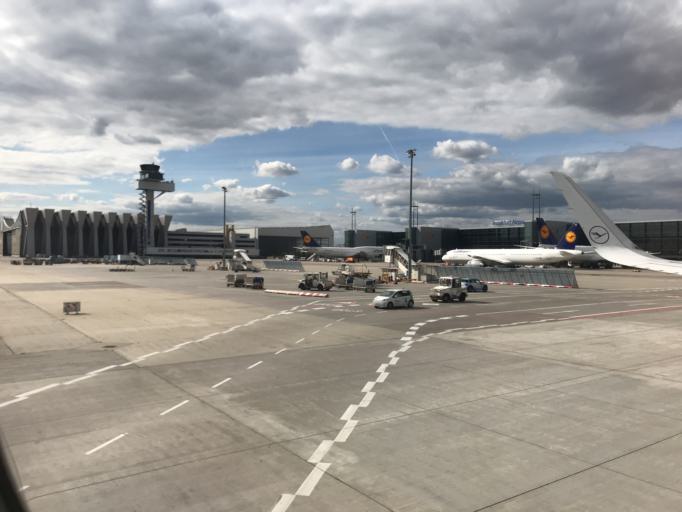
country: DE
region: Hesse
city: Kelsterbach
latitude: 50.0454
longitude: 8.5642
